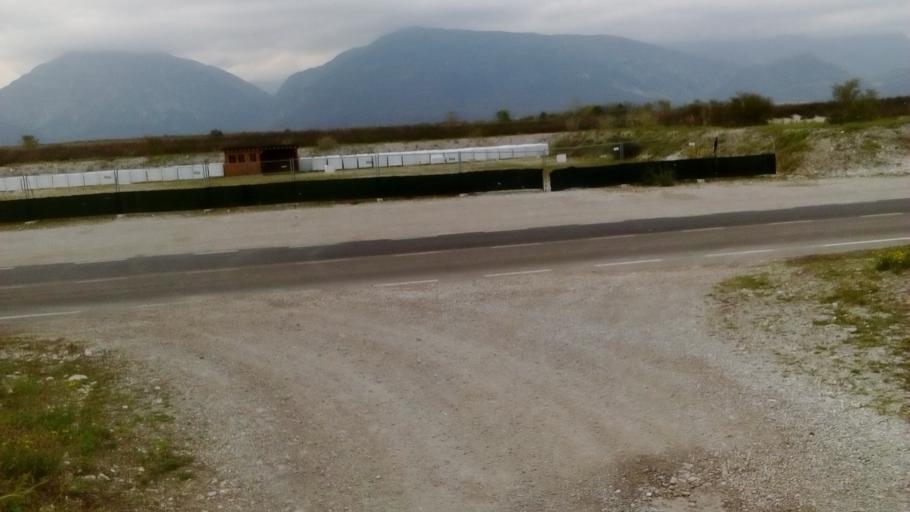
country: IT
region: Friuli Venezia Giulia
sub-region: Provincia di Pordenone
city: Vajont
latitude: 46.1249
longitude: 12.7232
